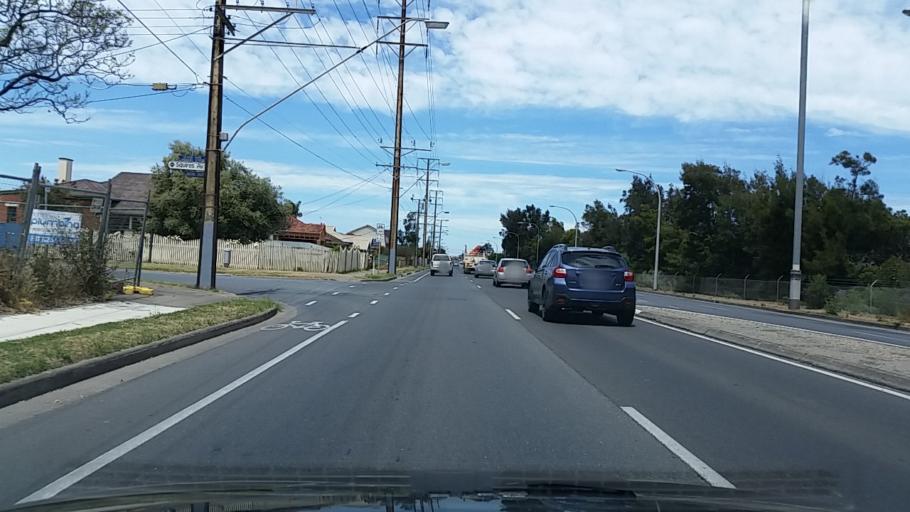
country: AU
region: South Australia
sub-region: Charles Sturt
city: Seaton
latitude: -34.8957
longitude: 138.5140
